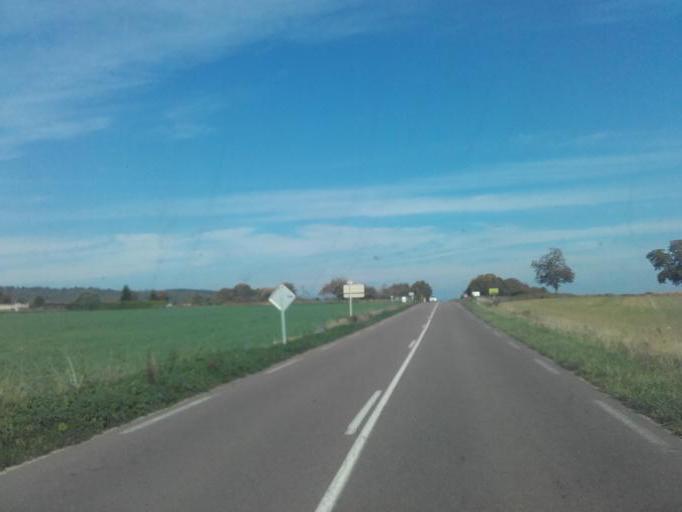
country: FR
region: Bourgogne
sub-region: Departement de Saone-et-Loire
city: Rully
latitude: 46.8699
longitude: 4.7524
